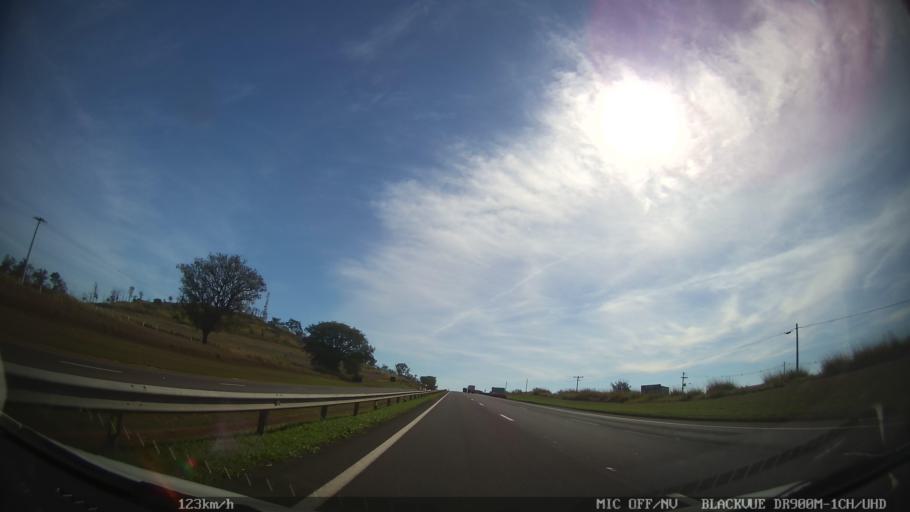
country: BR
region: Sao Paulo
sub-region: Leme
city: Leme
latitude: -22.1617
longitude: -47.3998
